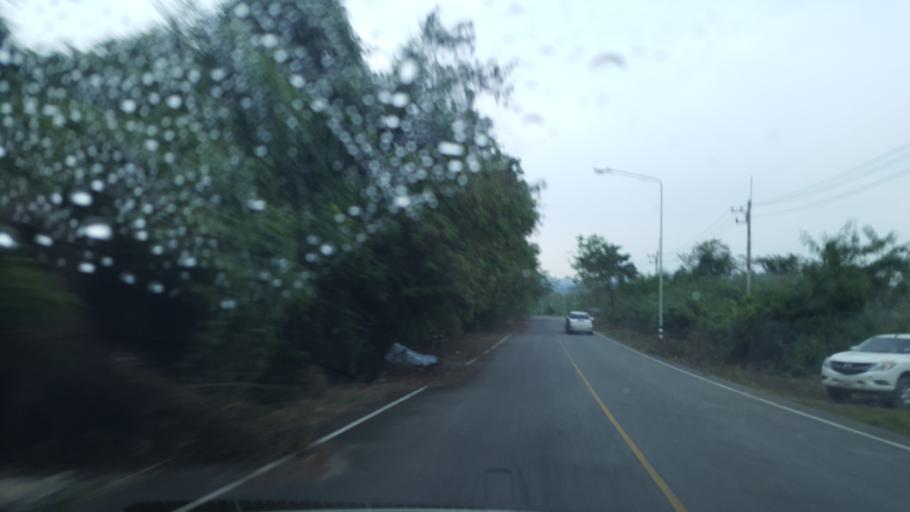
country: TH
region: Chon Buri
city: Ban Bueng
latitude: 13.2375
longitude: 101.0304
